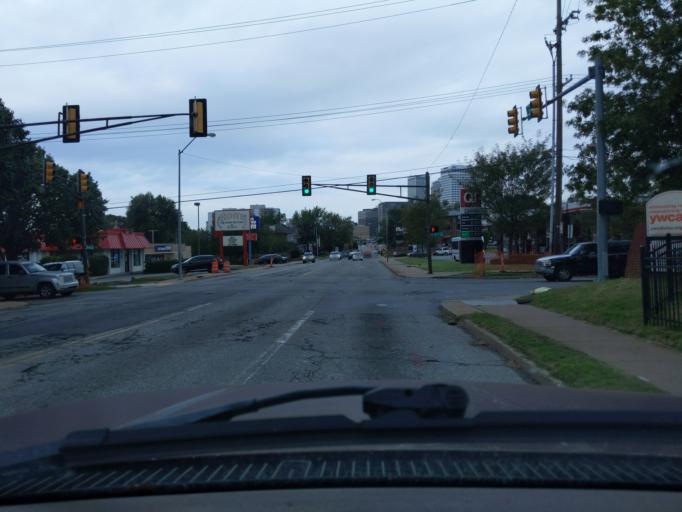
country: US
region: Oklahoma
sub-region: Tulsa County
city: Tulsa
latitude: 36.1404
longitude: -95.9924
